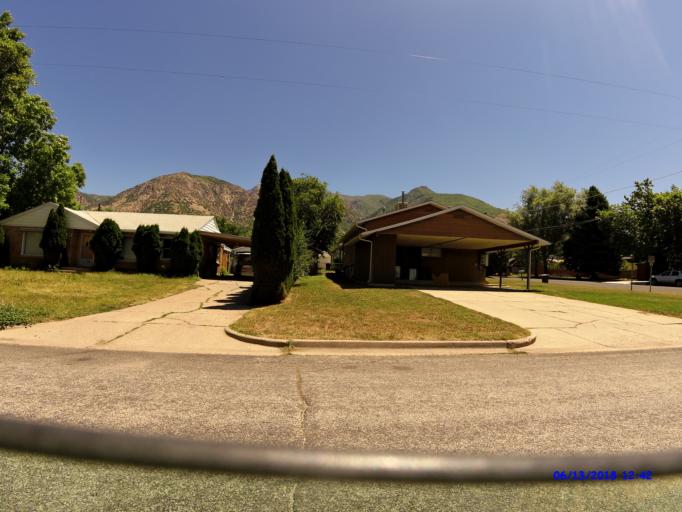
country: US
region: Utah
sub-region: Weber County
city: South Ogden
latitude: 41.1998
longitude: -111.9473
